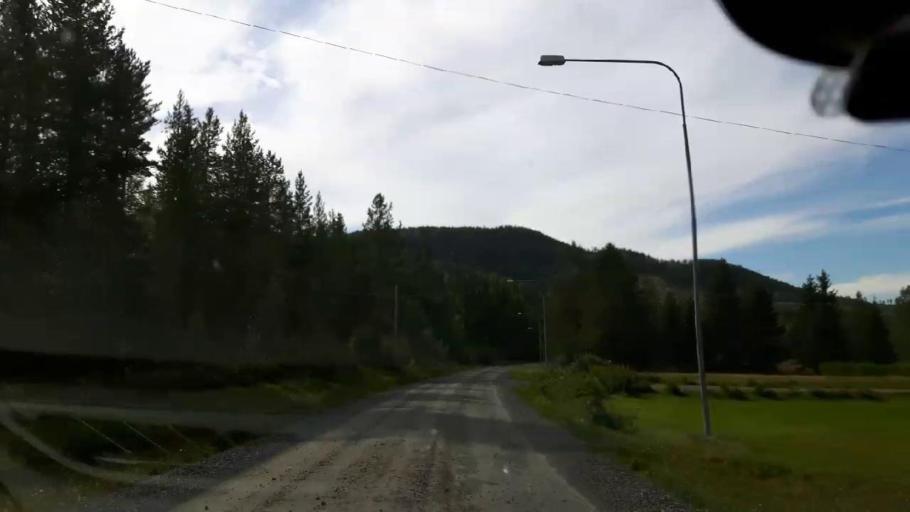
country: SE
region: Jaemtland
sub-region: Ragunda Kommun
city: Hammarstrand
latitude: 63.1329
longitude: 16.1354
